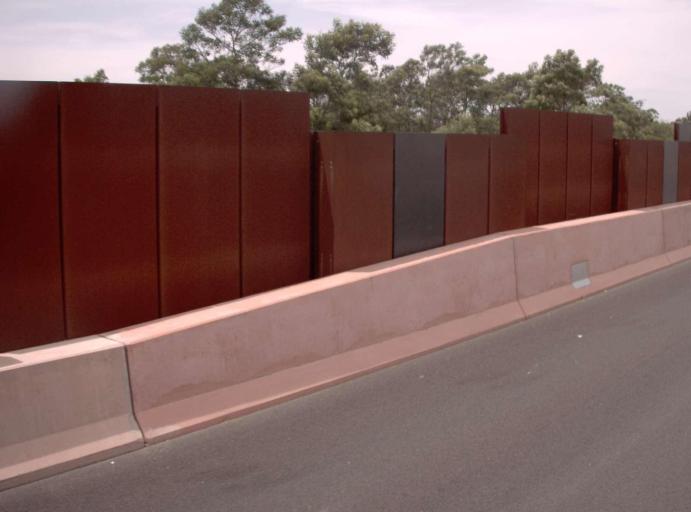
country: AU
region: Victoria
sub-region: Frankston
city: Carrum Downs
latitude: -38.1159
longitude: 145.1667
